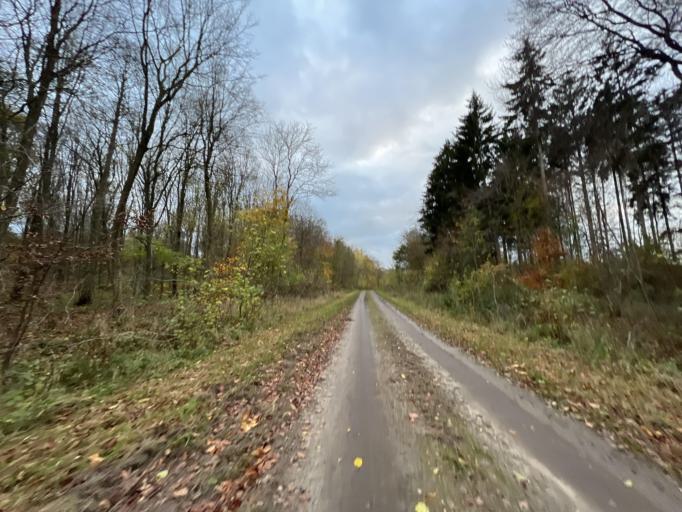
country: DE
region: Mecklenburg-Vorpommern
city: Putbus
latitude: 54.3644
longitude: 13.4436
